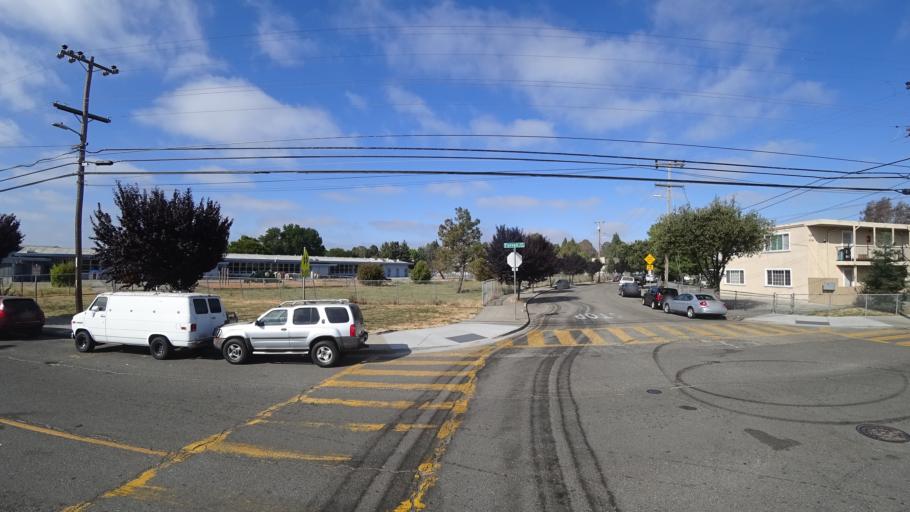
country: US
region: California
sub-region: Alameda County
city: Hayward
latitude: 37.6367
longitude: -122.0747
